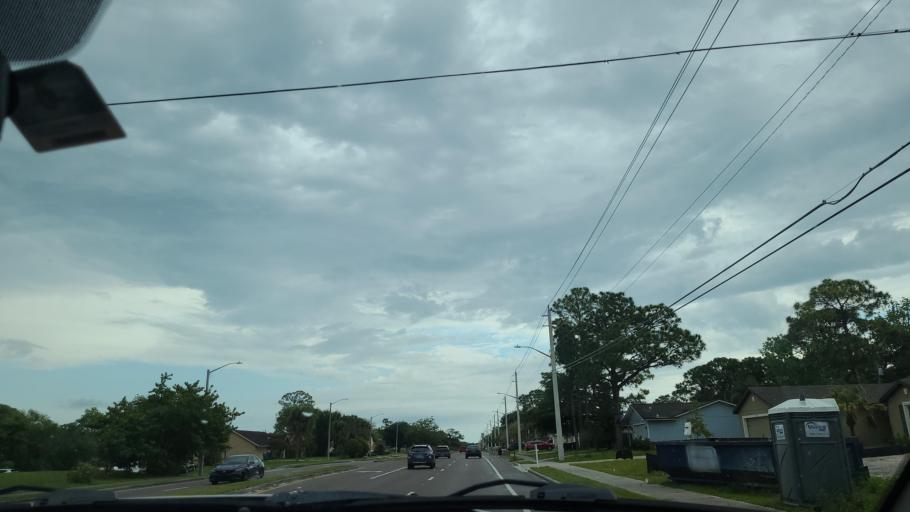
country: US
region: Florida
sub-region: Brevard County
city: June Park
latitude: 28.0318
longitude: -80.6878
